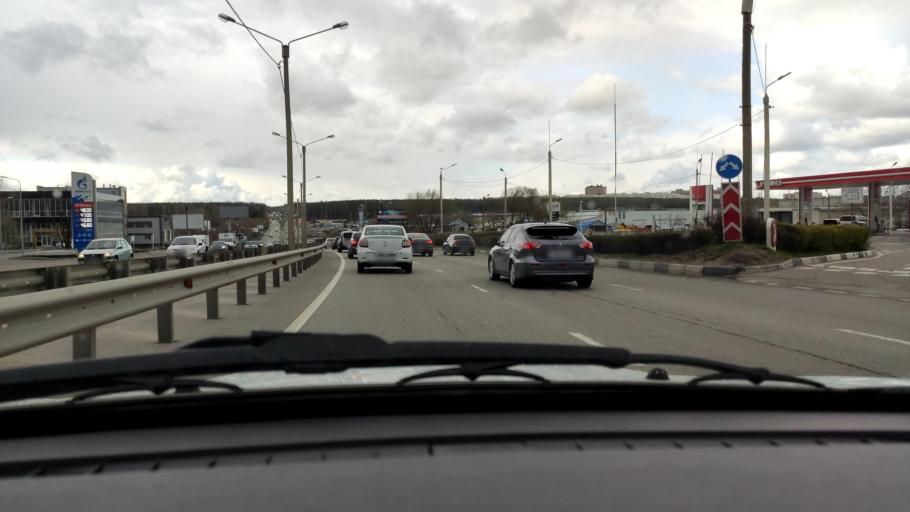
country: RU
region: Voronezj
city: Pridonskoy
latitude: 51.6663
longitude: 39.1257
